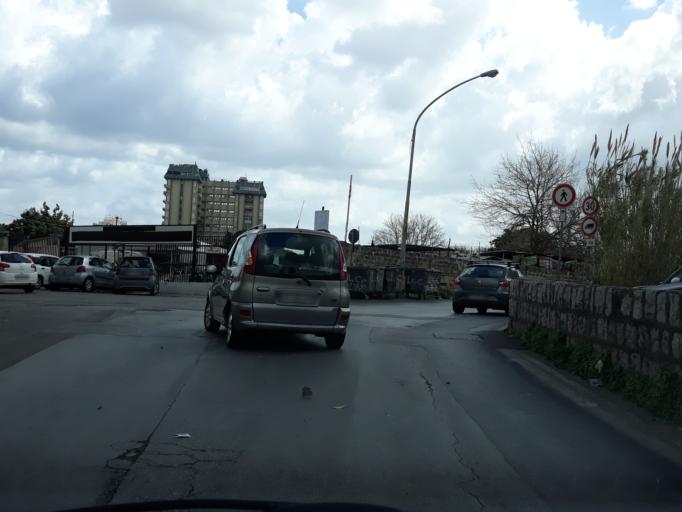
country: IT
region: Sicily
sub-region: Palermo
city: Palermo
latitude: 38.1259
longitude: 13.3142
